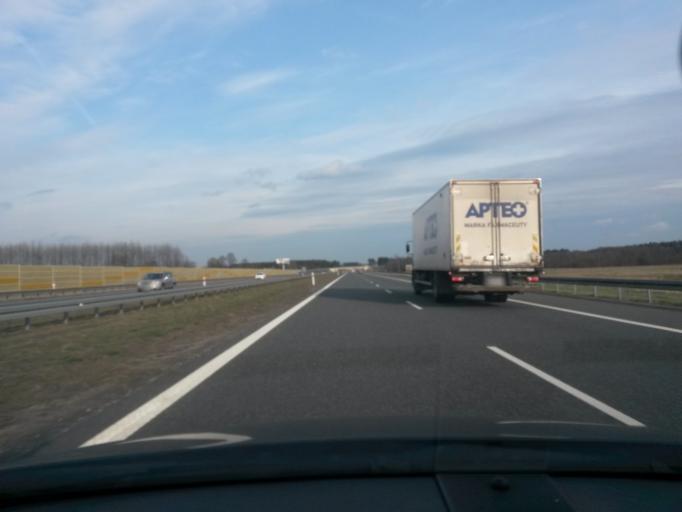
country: PL
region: Lodz Voivodeship
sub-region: Powiat zgierski
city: Ozorkow
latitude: 51.9370
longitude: 19.2531
